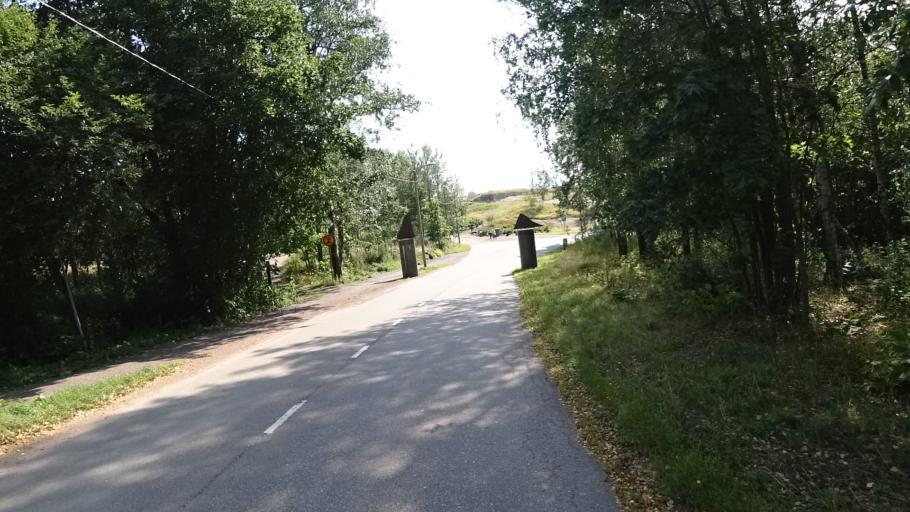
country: FI
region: Kymenlaakso
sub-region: Kotka-Hamina
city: Kotka
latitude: 60.4523
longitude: 26.9374
